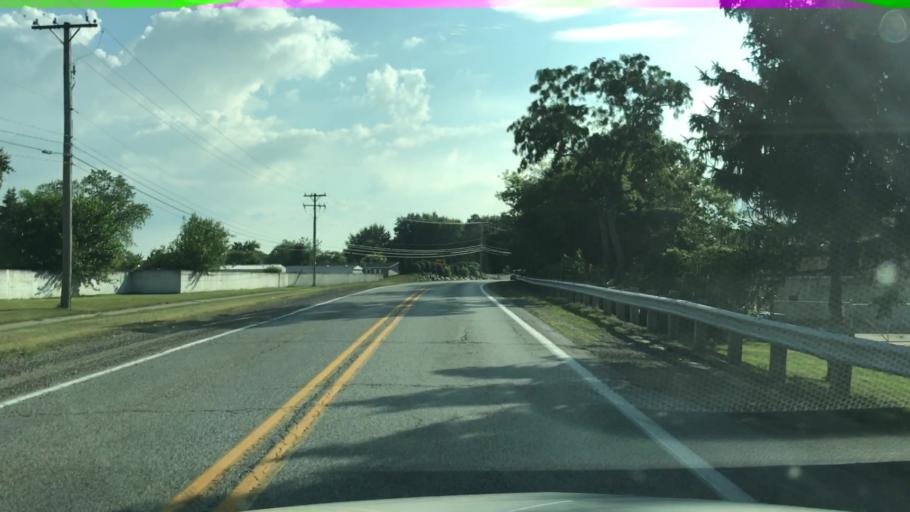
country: US
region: Michigan
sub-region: Macomb County
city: Fraser
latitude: 42.5776
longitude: -82.9591
